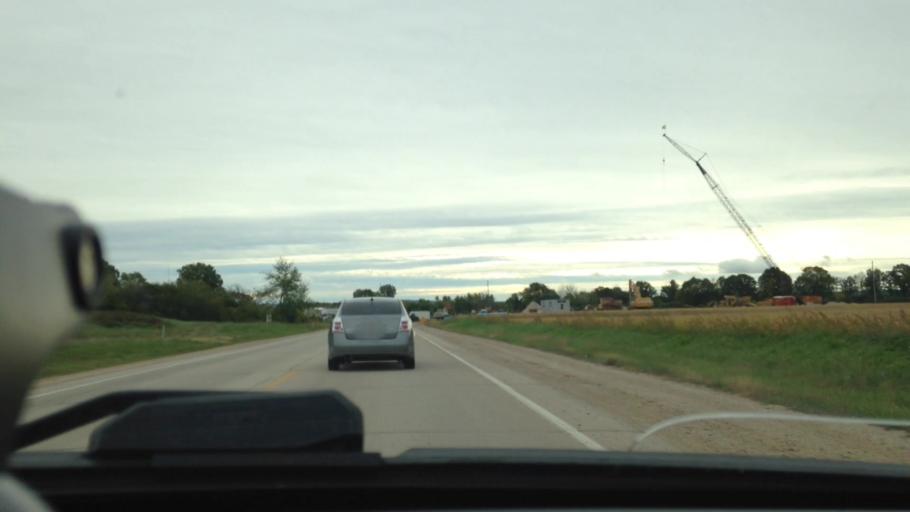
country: US
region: Wisconsin
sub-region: Fond du Lac County
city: North Fond du Lac
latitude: 43.7989
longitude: -88.4922
